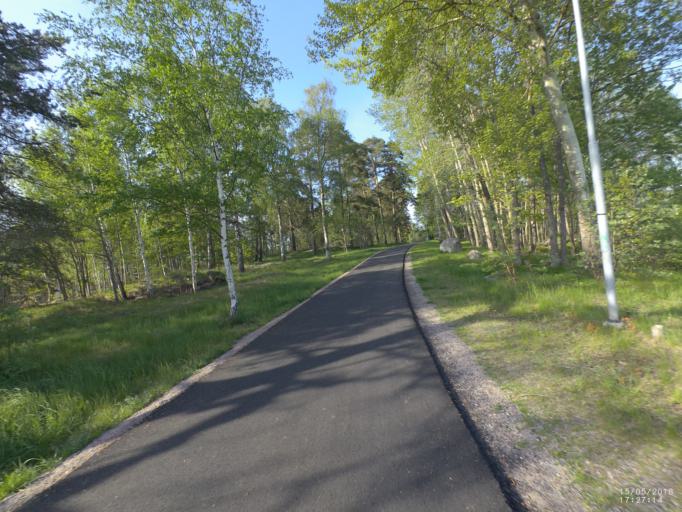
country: SE
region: Soedermanland
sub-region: Nykopings Kommun
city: Nykoping
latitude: 58.7241
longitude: 17.0245
